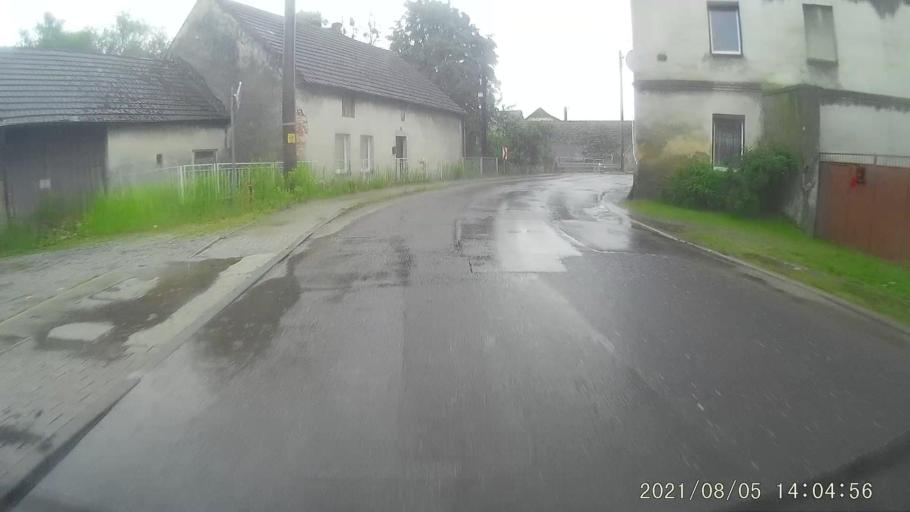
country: PL
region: Opole Voivodeship
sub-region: Powiat krapkowicki
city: Strzeleczki
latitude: 50.4622
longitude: 17.8555
